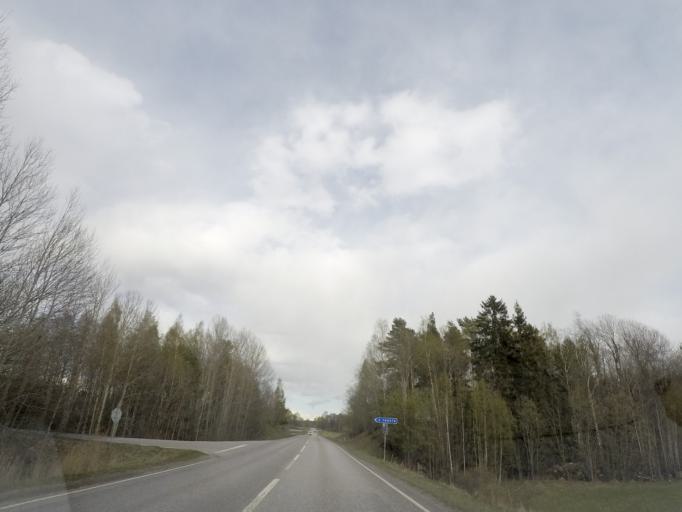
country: SE
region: Vaestmanland
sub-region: Kungsors Kommun
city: Kungsoer
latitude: 59.2850
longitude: 16.1523
